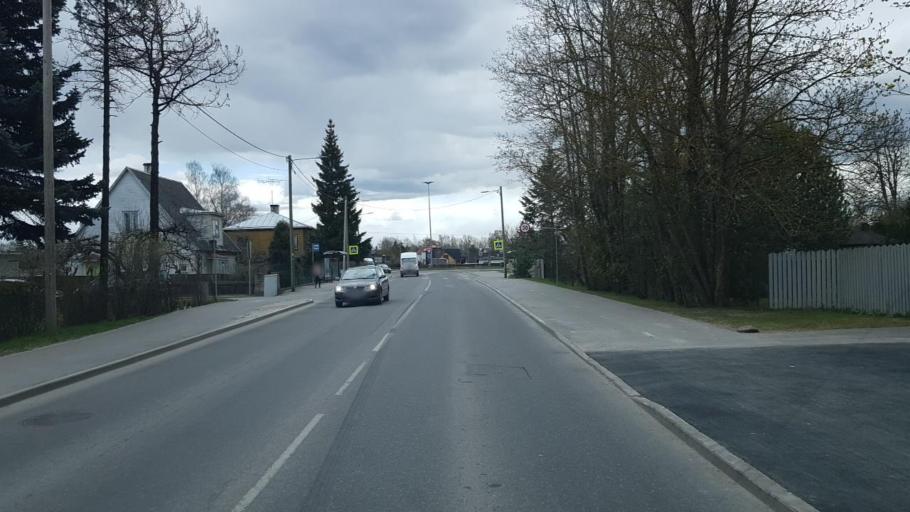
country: EE
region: Tartu
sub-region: Tartu linn
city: Tartu
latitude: 58.3557
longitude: 26.7068
